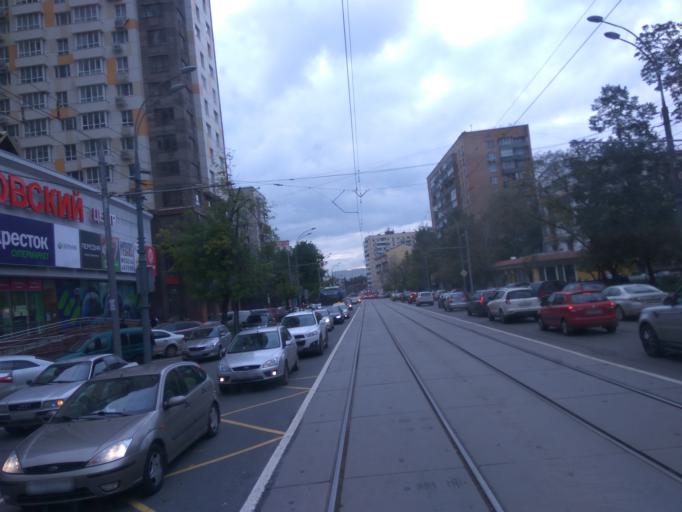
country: RU
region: Moskovskaya
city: Izmaylovo
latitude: 55.7930
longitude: 37.7874
